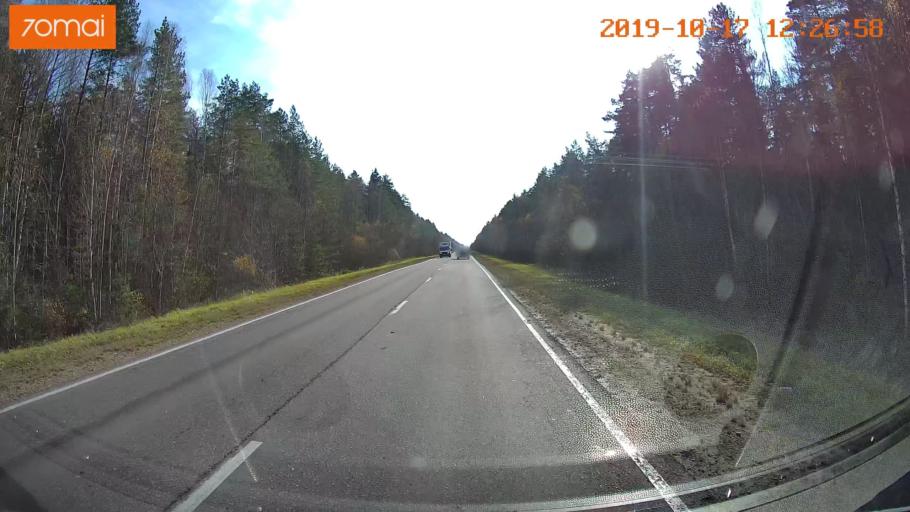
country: RU
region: Rjazan
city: Syntul
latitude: 55.0115
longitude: 41.2597
